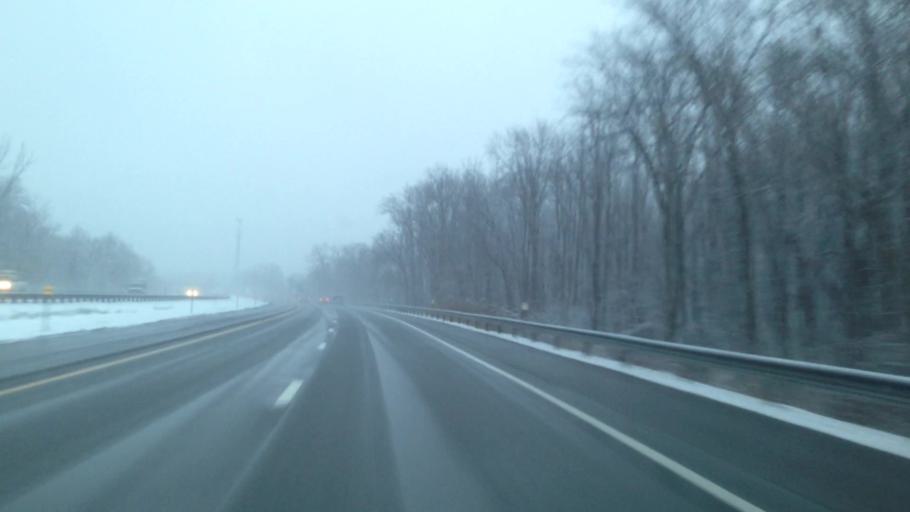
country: US
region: New York
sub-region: Madison County
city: Canastota
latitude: 43.0901
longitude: -75.7649
